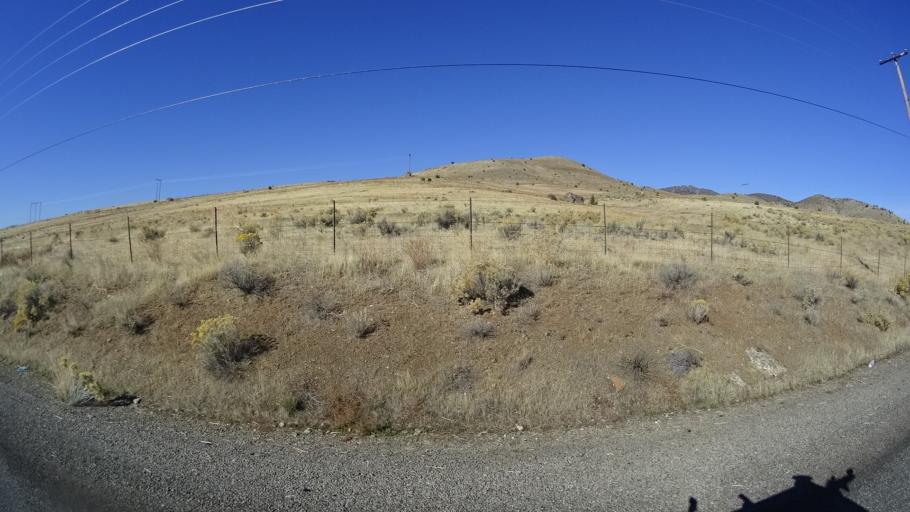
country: US
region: California
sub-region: Siskiyou County
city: Montague
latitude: 41.7794
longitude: -122.5217
